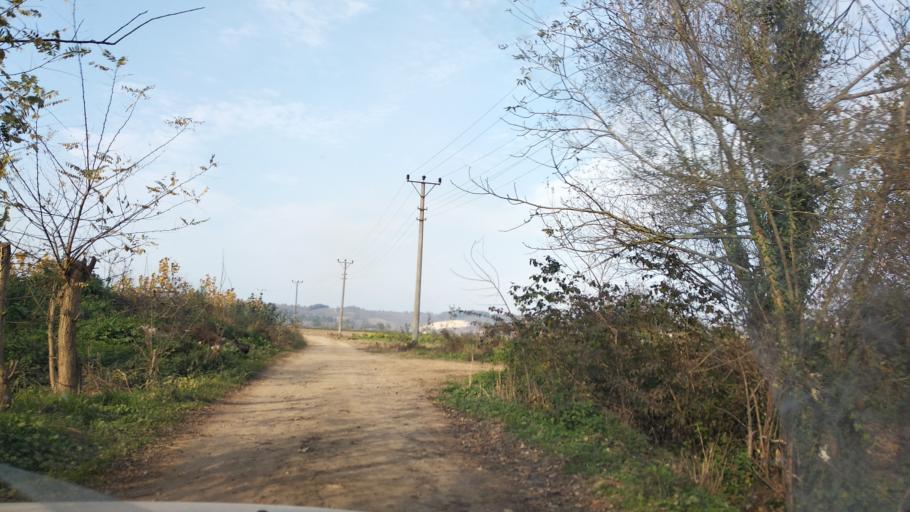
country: TR
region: Sakarya
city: Karasu
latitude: 41.0843
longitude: 30.6023
